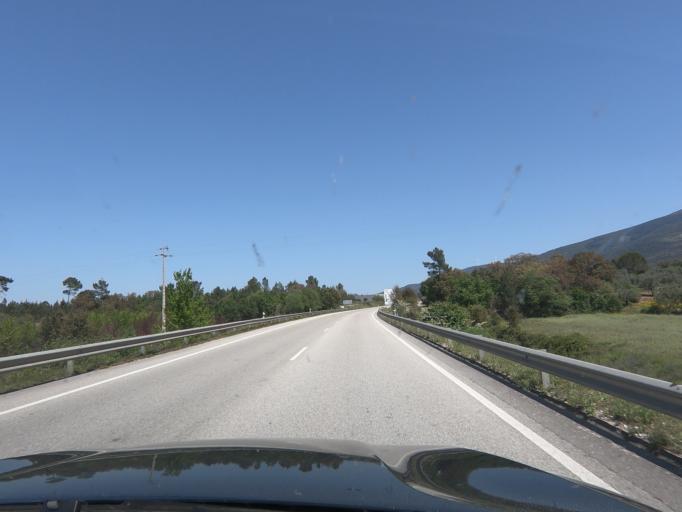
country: PT
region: Coimbra
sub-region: Lousa
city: Lousa
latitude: 40.1289
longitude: -8.2559
